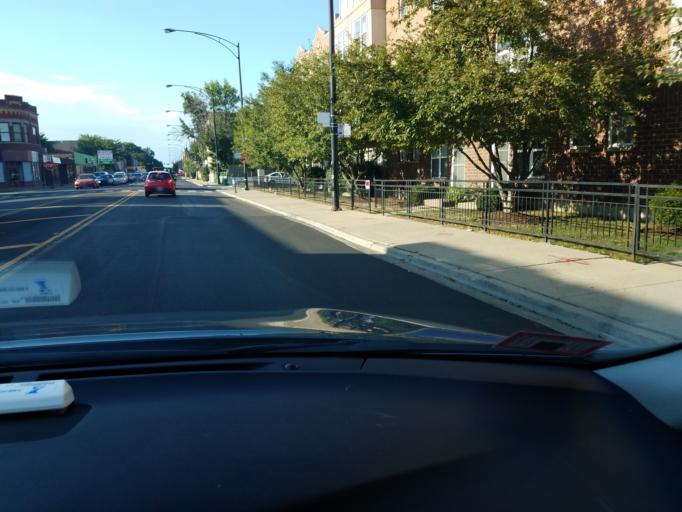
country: US
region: Illinois
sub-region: Cook County
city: Lincolnwood
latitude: 41.9696
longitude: -87.7280
